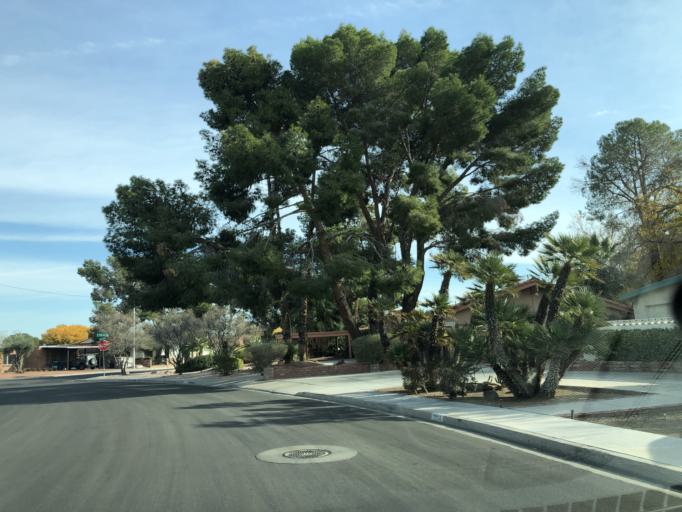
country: US
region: Nevada
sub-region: Clark County
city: Winchester
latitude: 36.1233
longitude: -115.1219
